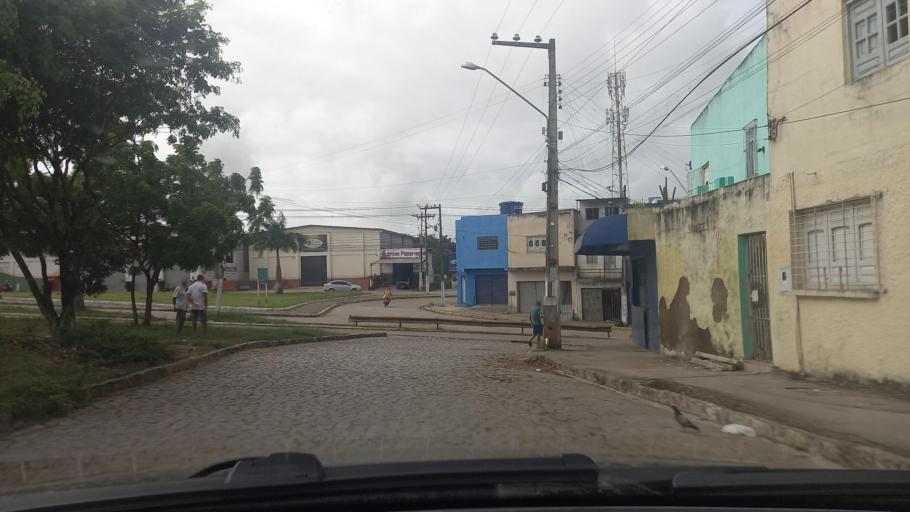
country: BR
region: Pernambuco
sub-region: Vitoria De Santo Antao
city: Vitoria de Santo Antao
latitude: -8.1153
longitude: -35.2968
